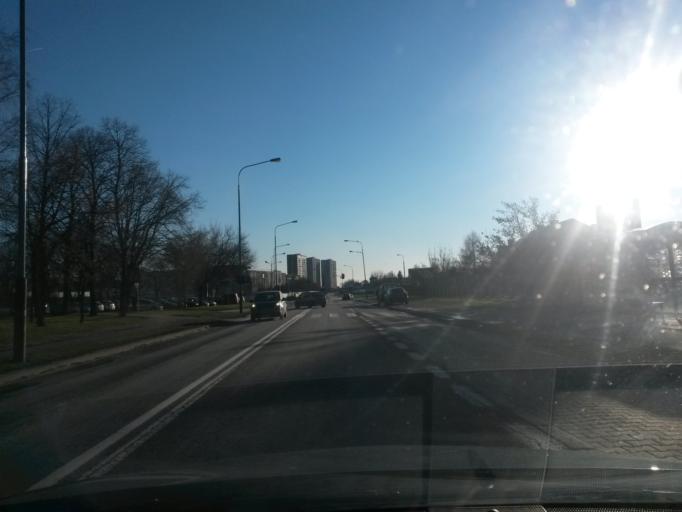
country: PL
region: Greater Poland Voivodeship
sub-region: Powiat poznanski
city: Suchy Las
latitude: 52.4518
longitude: 16.9120
